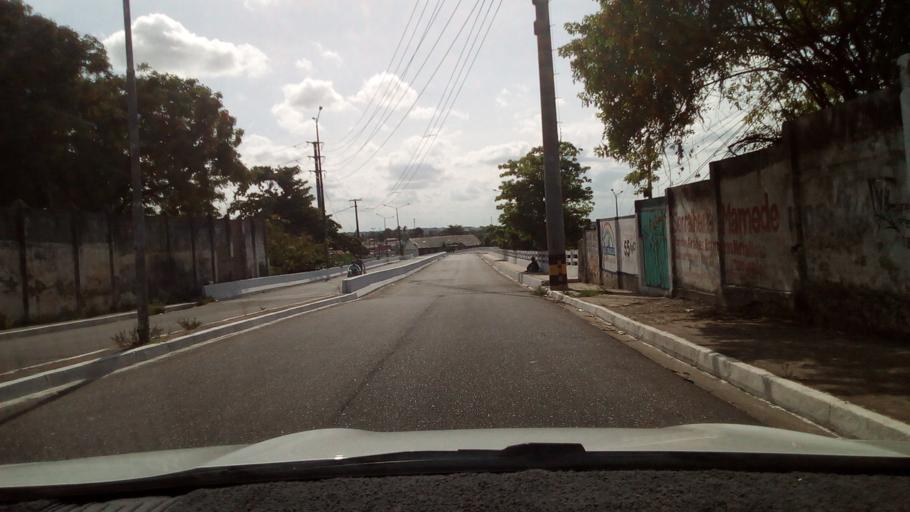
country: BR
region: Paraiba
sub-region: Joao Pessoa
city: Joao Pessoa
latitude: -7.1230
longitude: -34.8923
